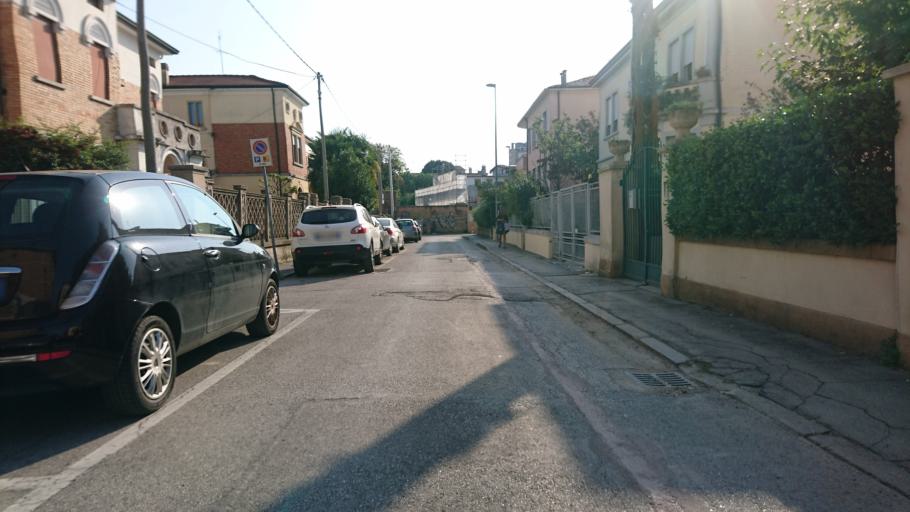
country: IT
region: Veneto
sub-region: Provincia di Padova
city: Padova
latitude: 45.4144
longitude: 11.8682
